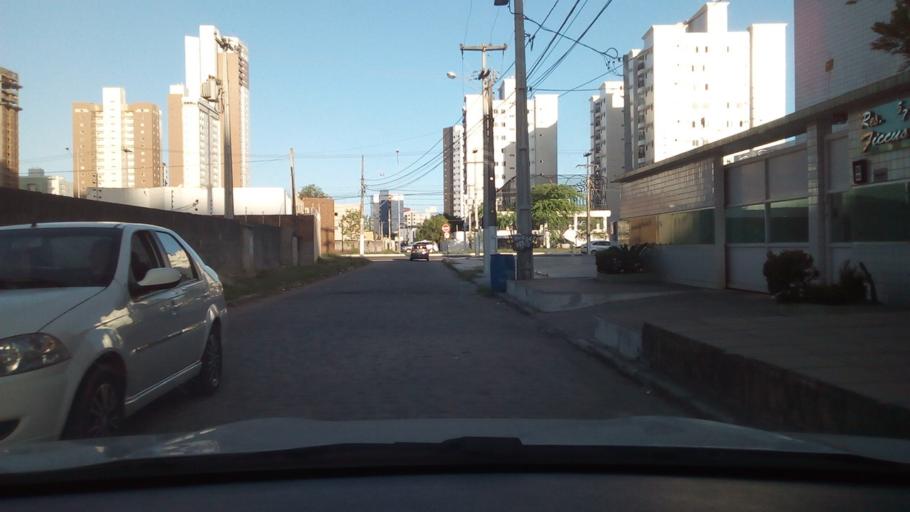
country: BR
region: Paraiba
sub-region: Joao Pessoa
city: Joao Pessoa
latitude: -7.0853
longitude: -34.8407
